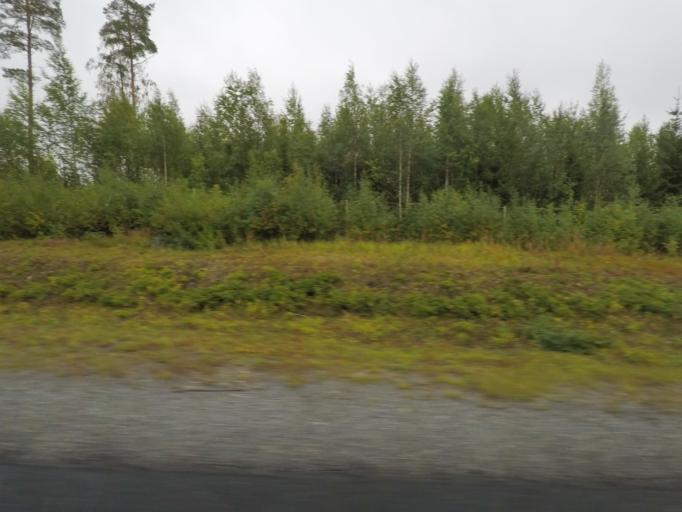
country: FI
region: Northern Savo
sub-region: Kuopio
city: Kuopio
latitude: 62.7750
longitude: 27.5883
